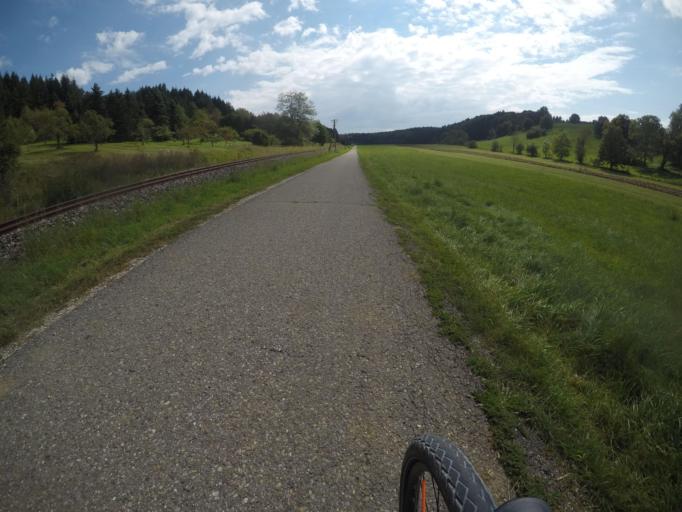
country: DE
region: Baden-Wuerttemberg
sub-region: Tuebingen Region
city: Munsingen
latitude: 48.4002
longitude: 9.4953
